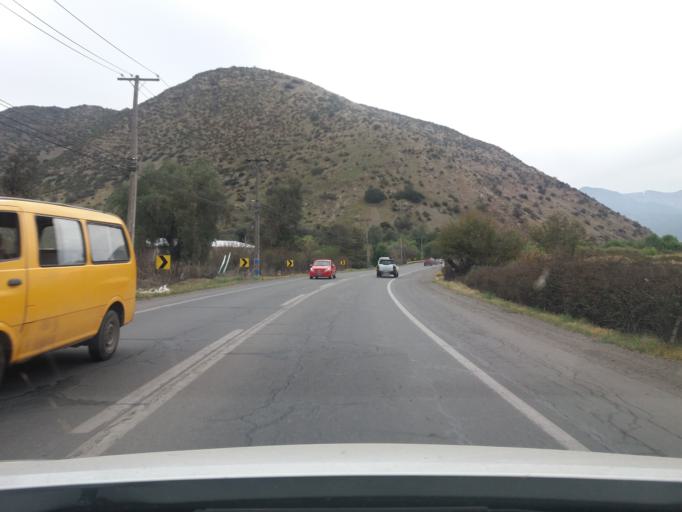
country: CL
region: Valparaiso
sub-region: Provincia de San Felipe
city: San Felipe
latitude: -32.7646
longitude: -70.7336
